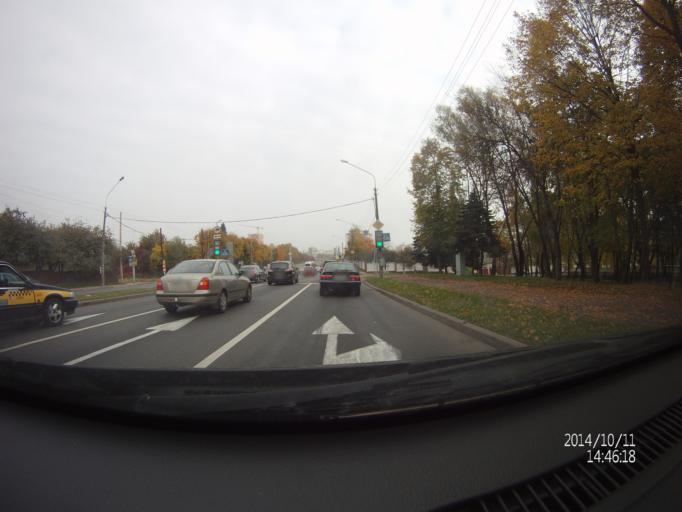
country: BY
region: Minsk
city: Minsk
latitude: 53.8723
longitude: 27.5479
